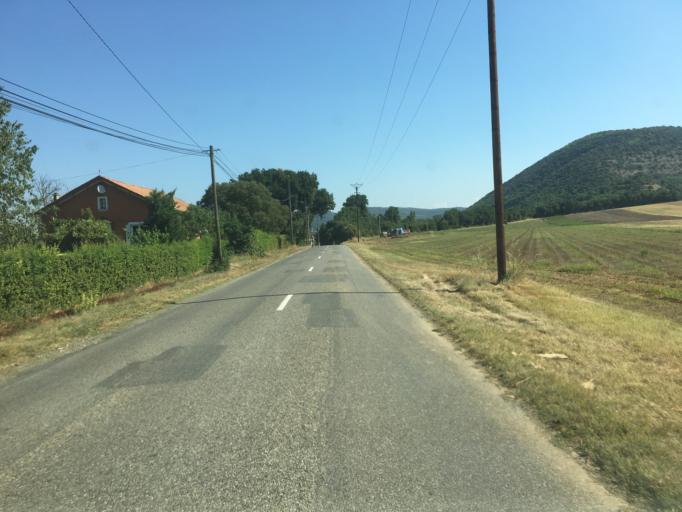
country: FR
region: Provence-Alpes-Cote d'Azur
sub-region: Departement des Alpes-de-Haute-Provence
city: Villeneuve
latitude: 43.8678
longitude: 5.8986
